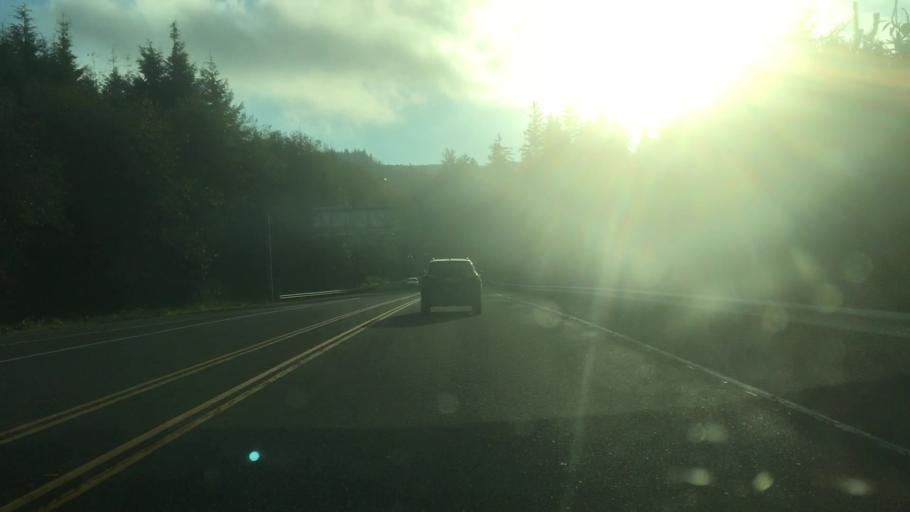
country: US
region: Oregon
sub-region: Clatsop County
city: Seaside
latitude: 45.9369
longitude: -123.9230
